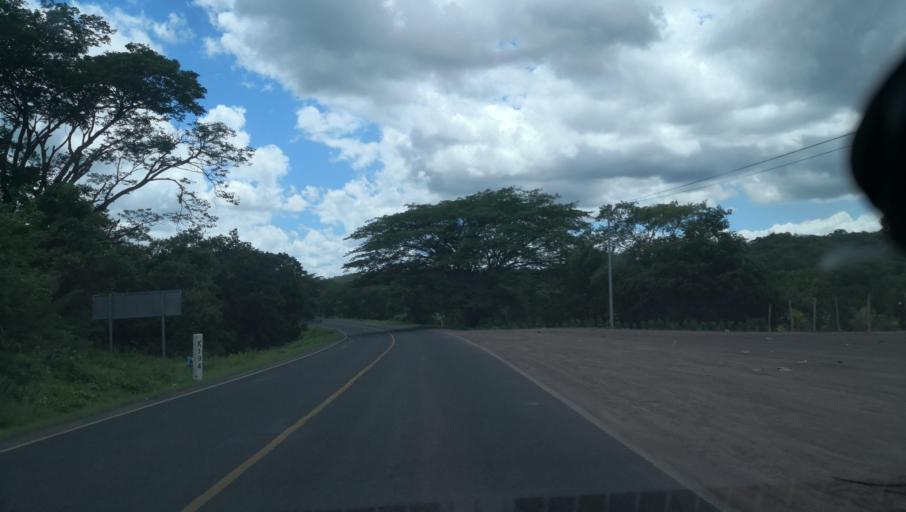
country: NI
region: Madriz
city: Palacaguina
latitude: 13.4341
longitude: -86.4146
